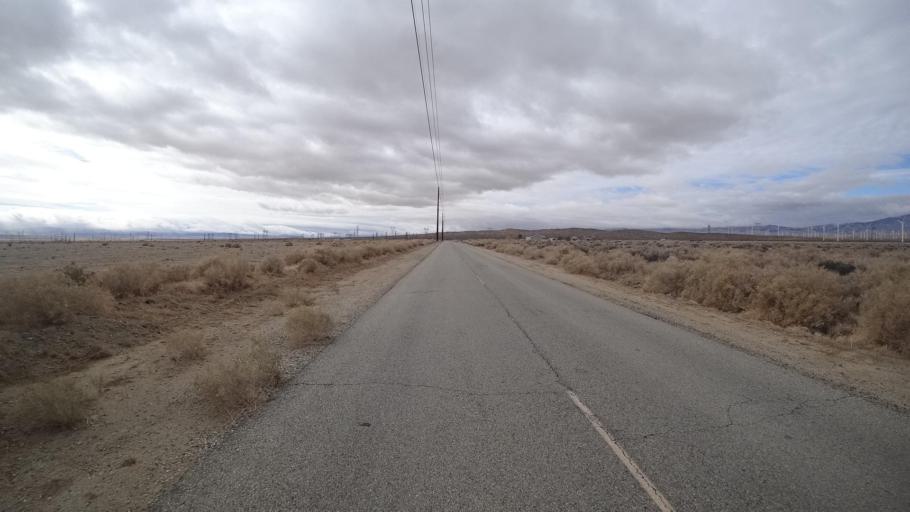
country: US
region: California
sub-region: Los Angeles County
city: Green Valley
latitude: 34.8626
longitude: -118.4173
